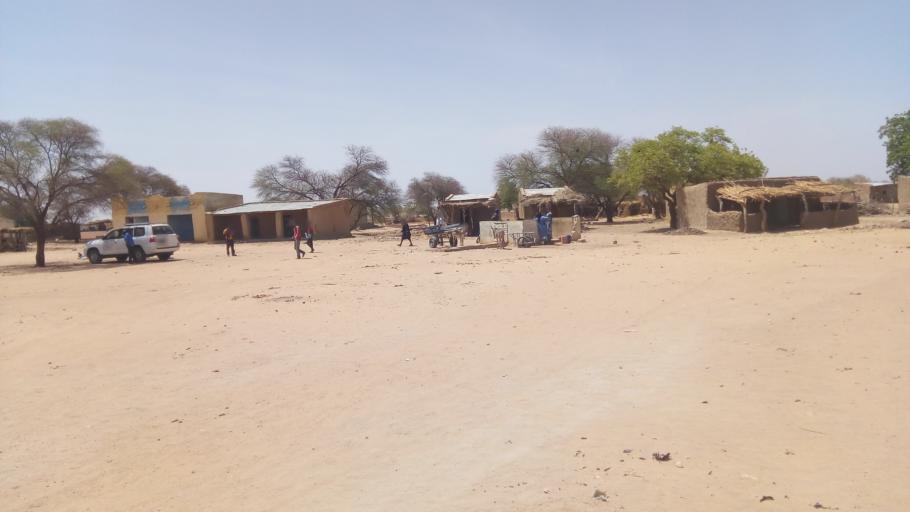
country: ML
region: Kayes
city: Diema
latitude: 14.5094
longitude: -8.8440
